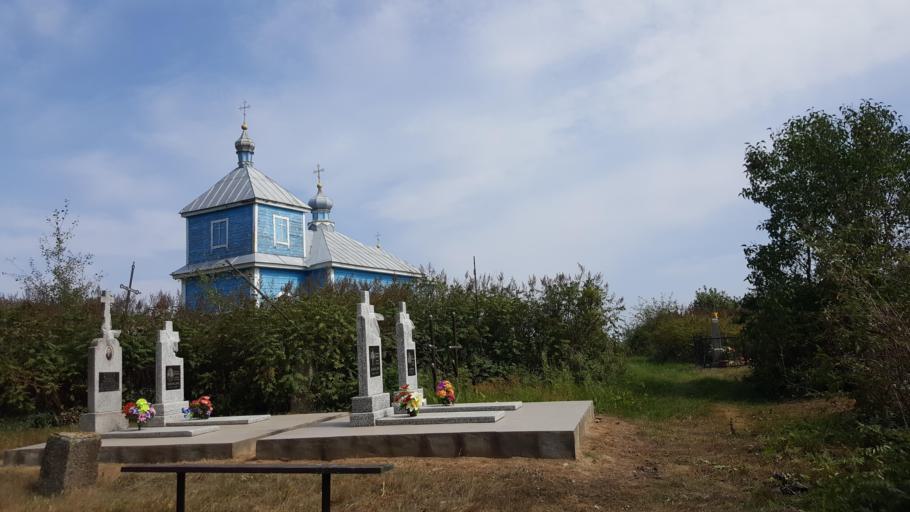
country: BY
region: Brest
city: Kamyanyets
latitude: 52.4574
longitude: 23.6529
